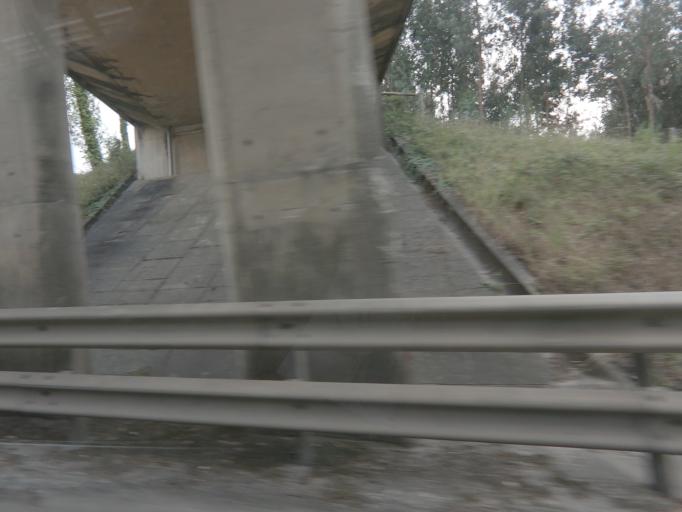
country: PT
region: Coimbra
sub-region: Penacova
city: Lorvao
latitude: 40.2992
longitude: -8.3120
